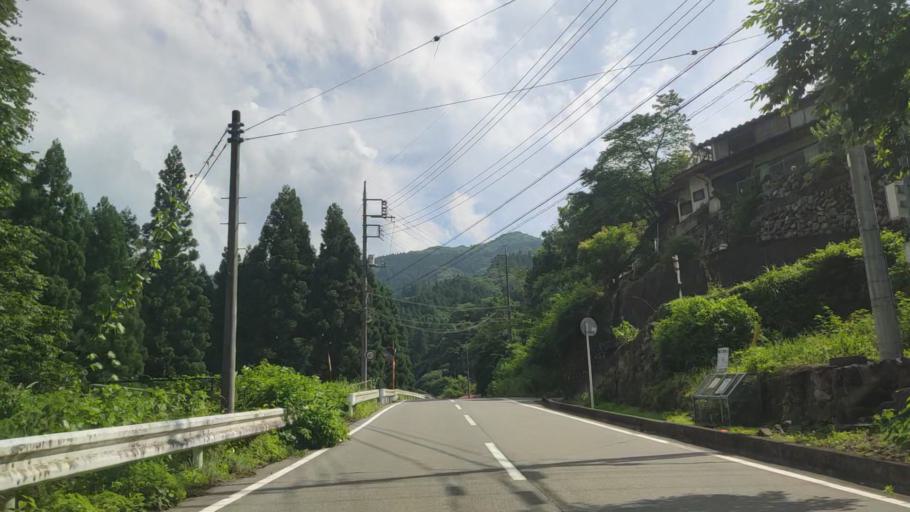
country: JP
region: Gunma
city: Tomioka
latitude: 36.1576
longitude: 138.7287
